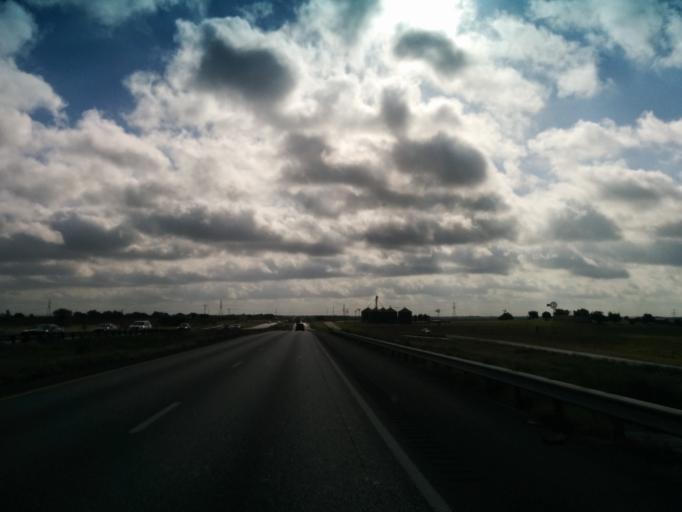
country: US
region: Texas
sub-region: Guadalupe County
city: McQueeney
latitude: 29.5403
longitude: -98.0723
